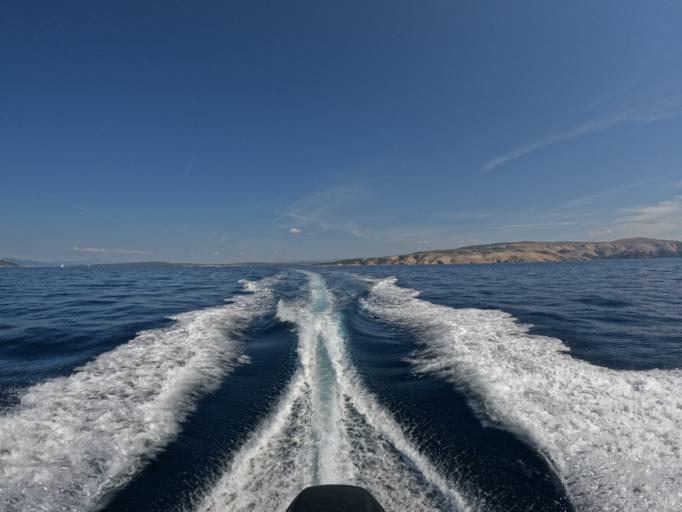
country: HR
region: Primorsko-Goranska
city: Punat
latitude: 44.9349
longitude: 14.6164
